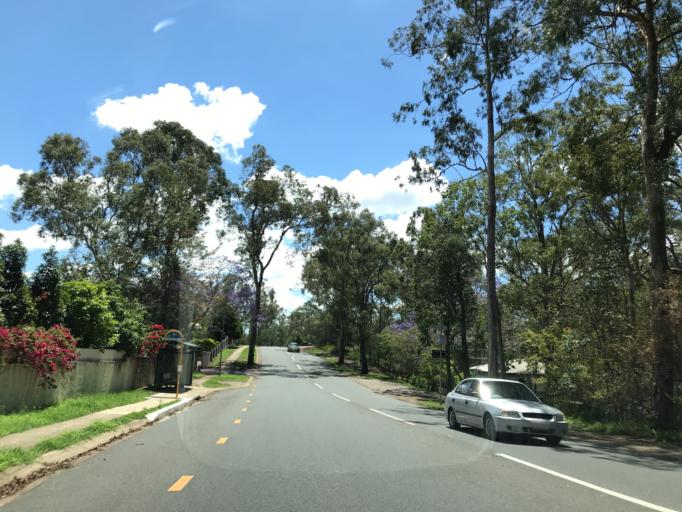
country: AU
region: Queensland
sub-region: Brisbane
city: Seventeen Mile Rocks
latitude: -27.5246
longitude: 152.9560
